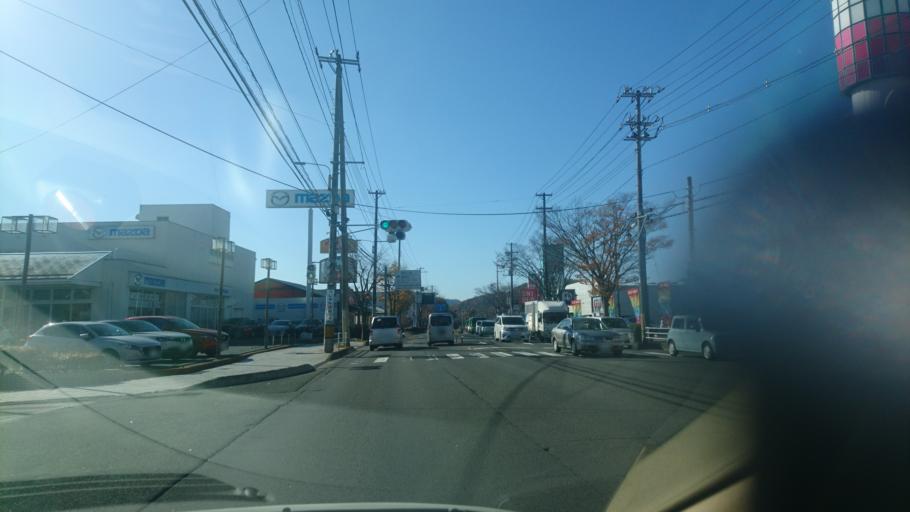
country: JP
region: Miyagi
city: Sendai
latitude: 38.2862
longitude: 140.8186
